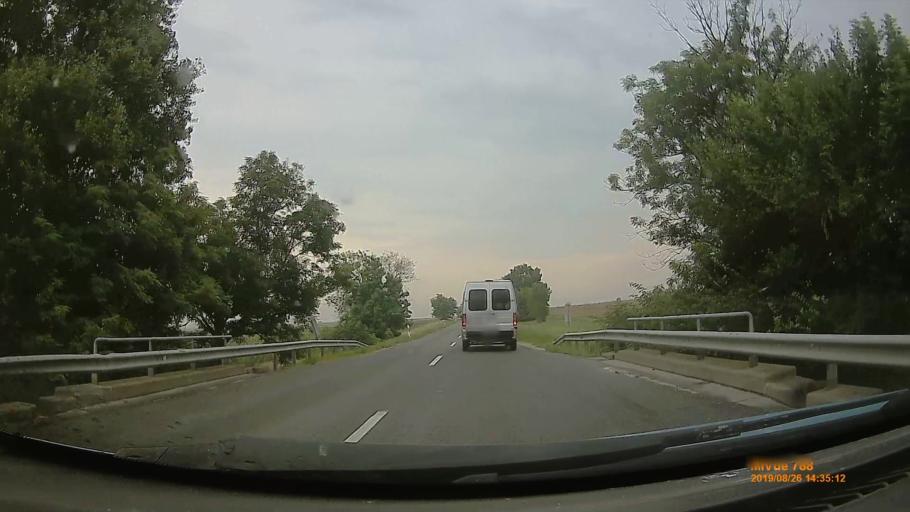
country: HU
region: Fejer
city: Szekesfehervar
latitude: 47.2505
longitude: 18.4187
